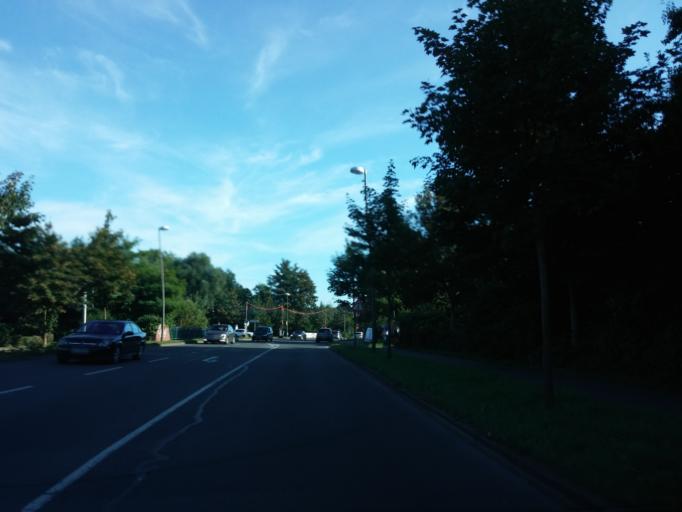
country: DE
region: North Rhine-Westphalia
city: Dorsten
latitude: 51.6749
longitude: 6.9617
